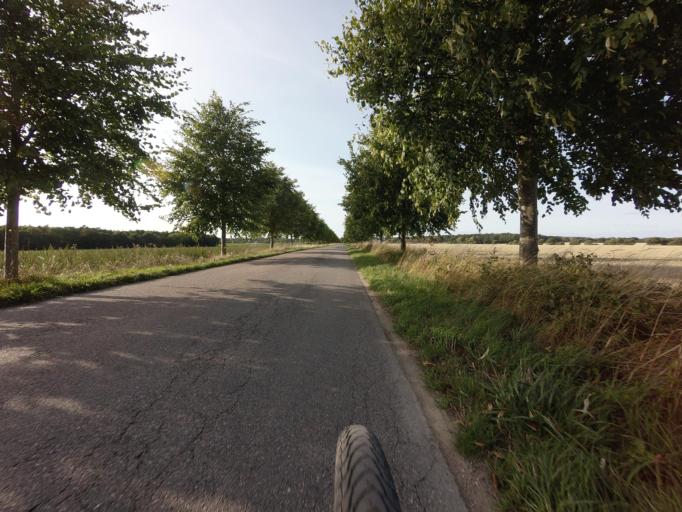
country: DK
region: Zealand
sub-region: Faxe Kommune
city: Fakse Ladeplads
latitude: 55.2443
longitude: 12.2321
